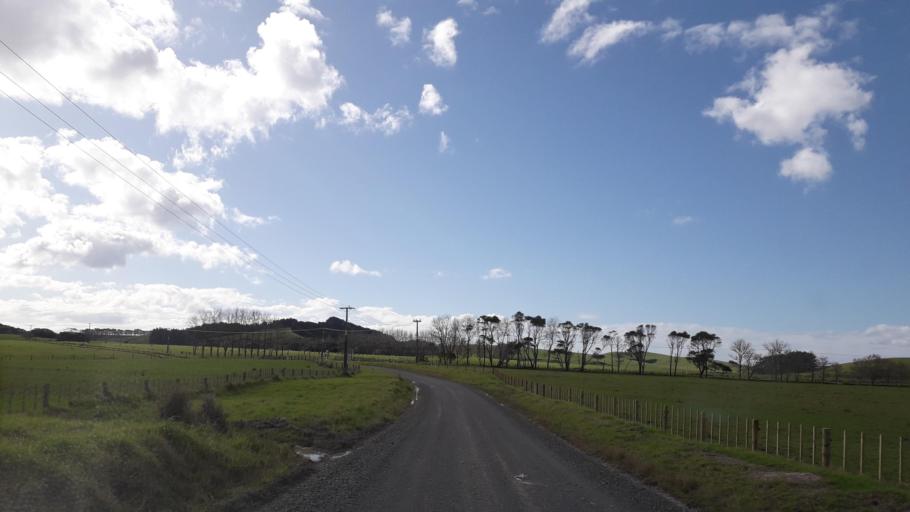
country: NZ
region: Northland
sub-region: Far North District
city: Kerikeri
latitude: -35.1415
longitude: 174.0369
